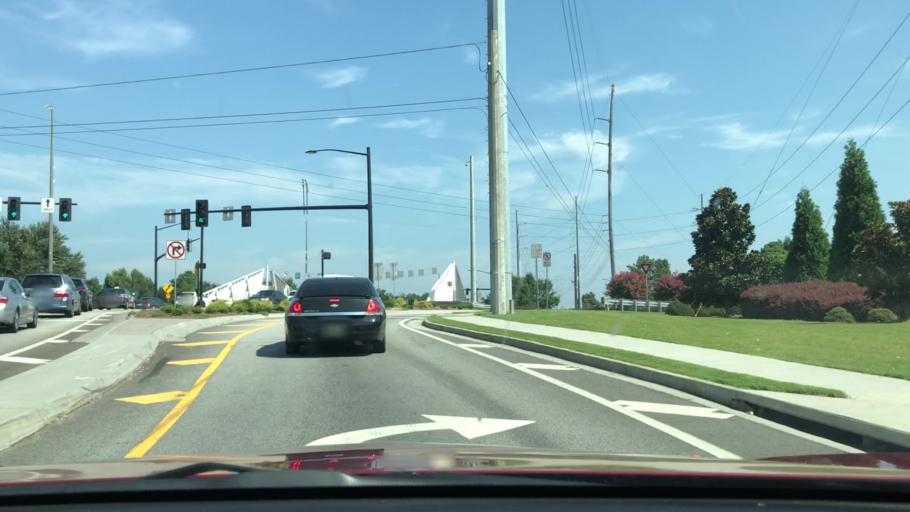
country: US
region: Georgia
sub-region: Gwinnett County
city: Norcross
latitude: 33.9111
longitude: -84.2071
